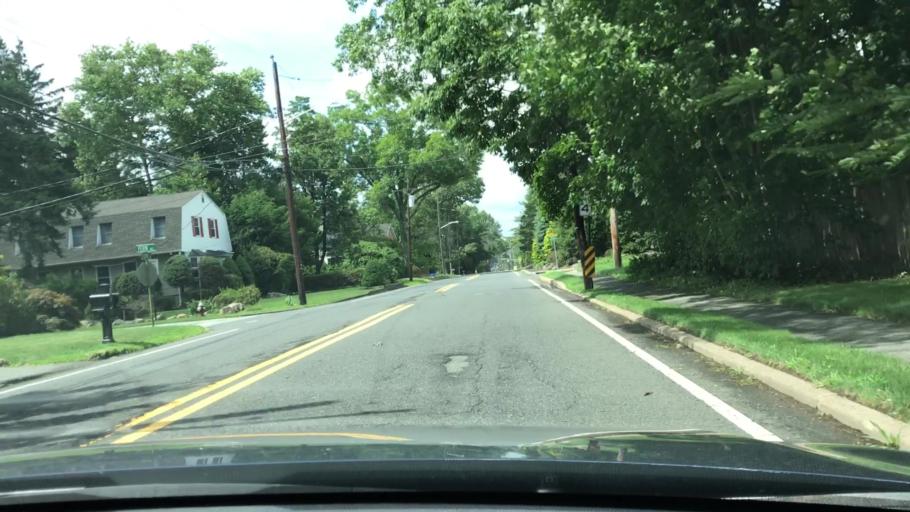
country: US
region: New Jersey
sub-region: Bergen County
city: Wyckoff
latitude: 41.0164
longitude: -74.1668
